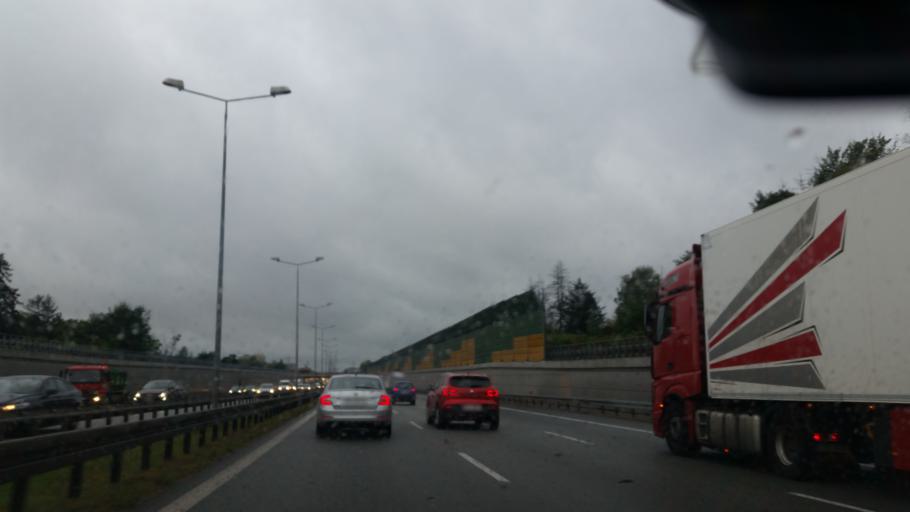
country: PL
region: Masovian Voivodeship
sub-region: Warszawa
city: Bemowo
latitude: 52.2486
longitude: 20.9301
